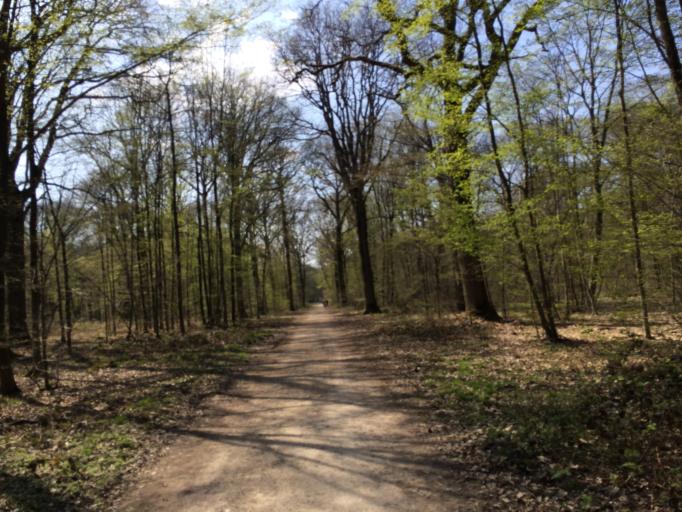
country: FR
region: Ile-de-France
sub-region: Departement de l'Essonne
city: Draveil
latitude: 48.6737
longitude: 2.4331
